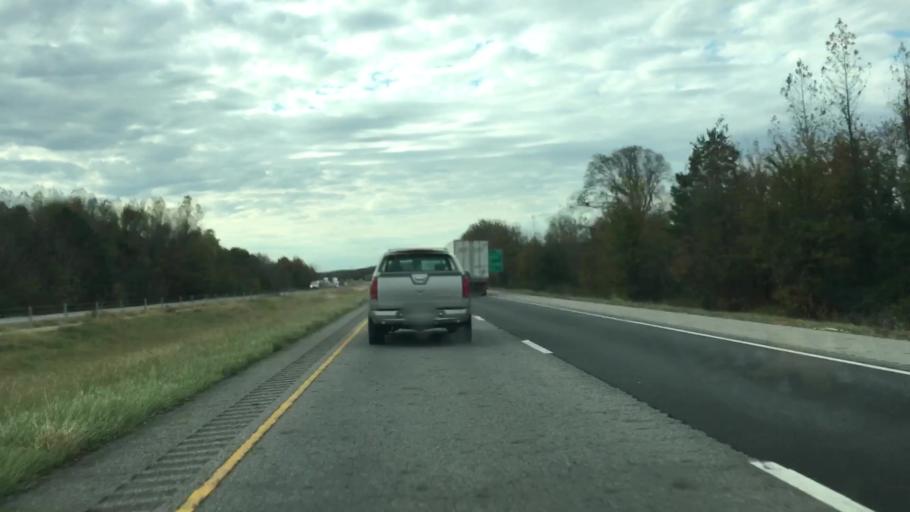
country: US
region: Arkansas
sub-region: Conway County
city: Morrilton
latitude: 35.1630
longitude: -92.6179
